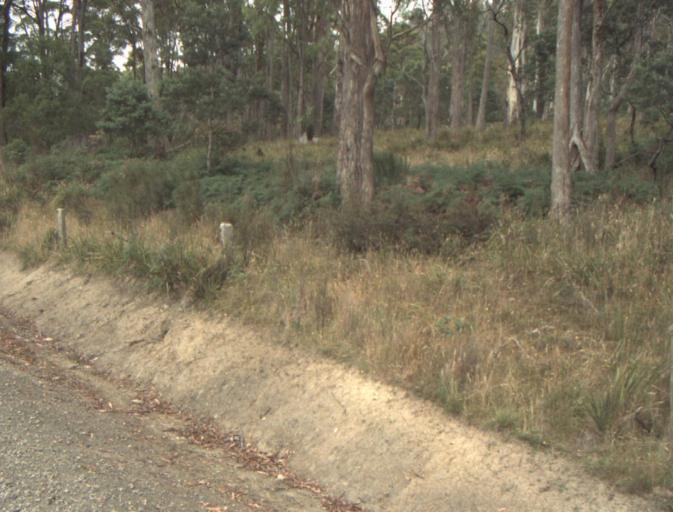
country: AU
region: Tasmania
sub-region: Northern Midlands
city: Evandale
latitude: -41.4652
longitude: 147.4484
